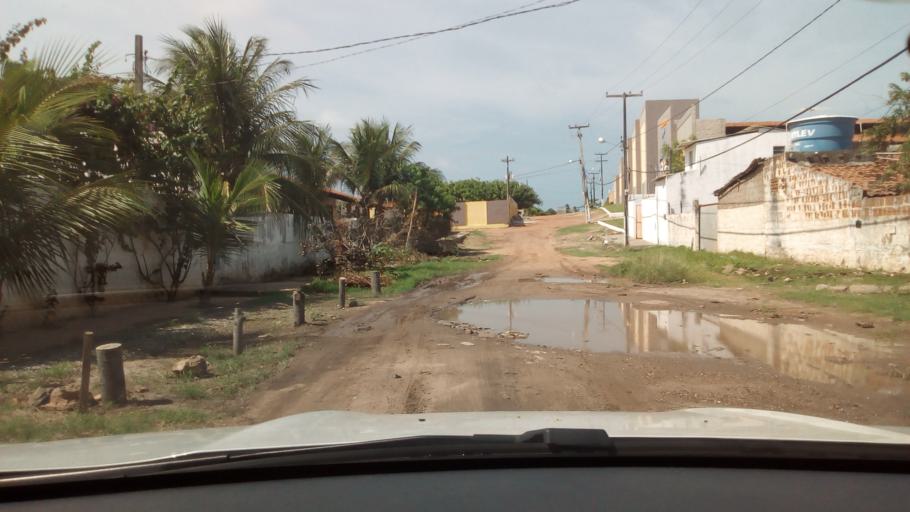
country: BR
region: Paraiba
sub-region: Conde
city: Conde
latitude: -7.2947
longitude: -34.8022
